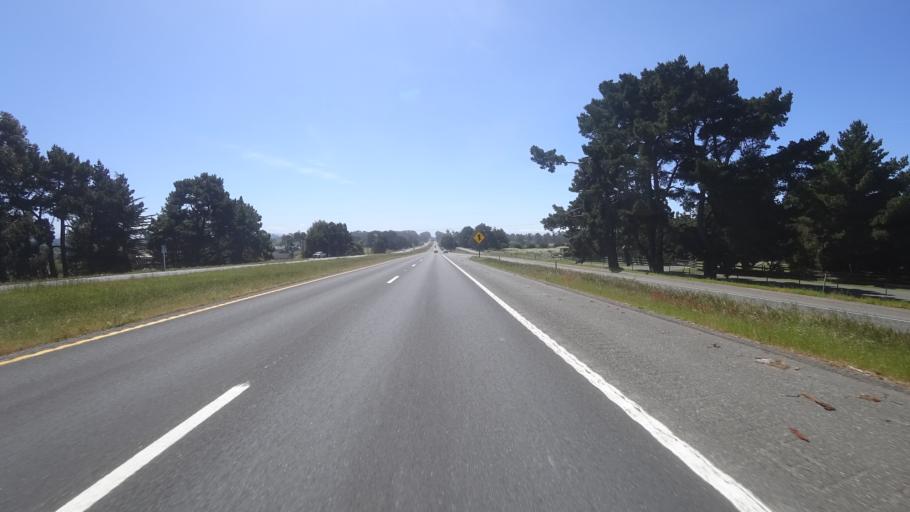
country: US
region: California
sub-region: Humboldt County
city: McKinleyville
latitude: 40.9683
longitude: -124.1162
